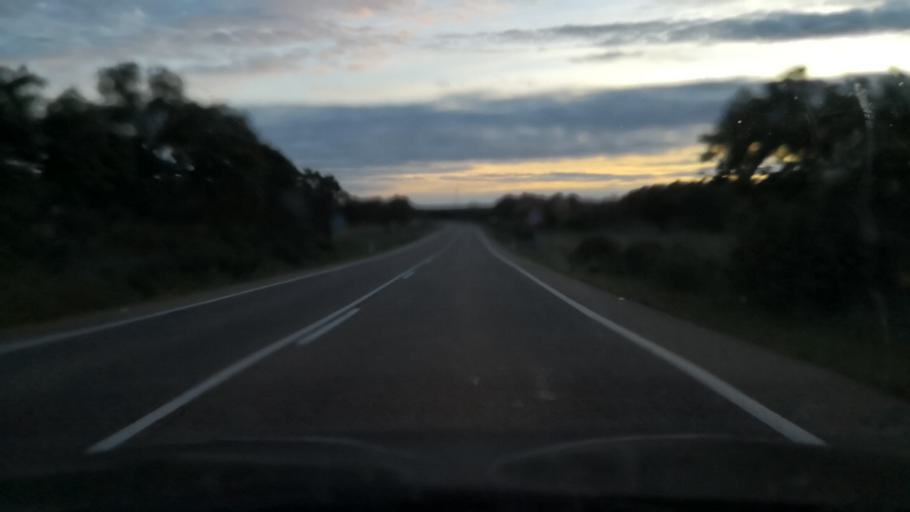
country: ES
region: Extremadura
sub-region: Provincia de Badajoz
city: Villar del Rey
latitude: 39.0397
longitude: -6.8124
